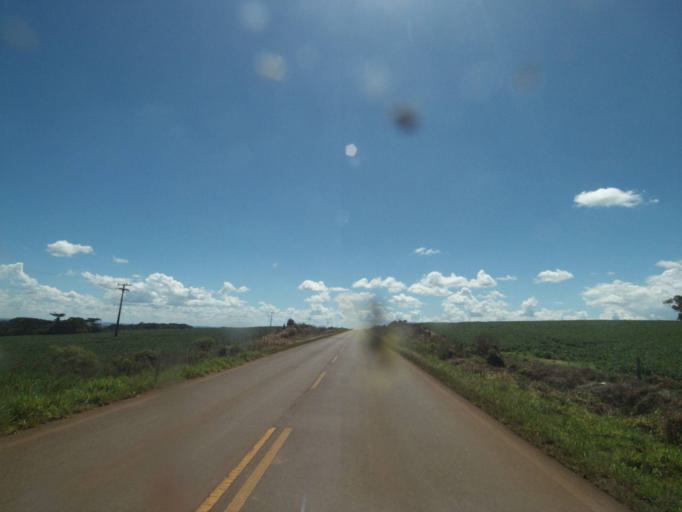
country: BR
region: Parana
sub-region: Pinhao
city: Pinhao
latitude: -25.8131
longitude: -52.0566
